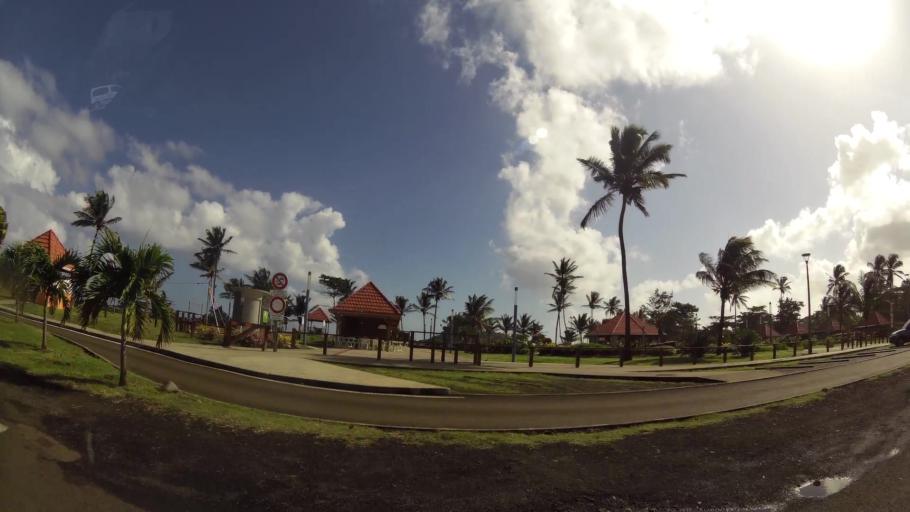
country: MQ
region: Martinique
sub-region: Martinique
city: Sainte-Marie
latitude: 14.7863
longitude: -60.9974
